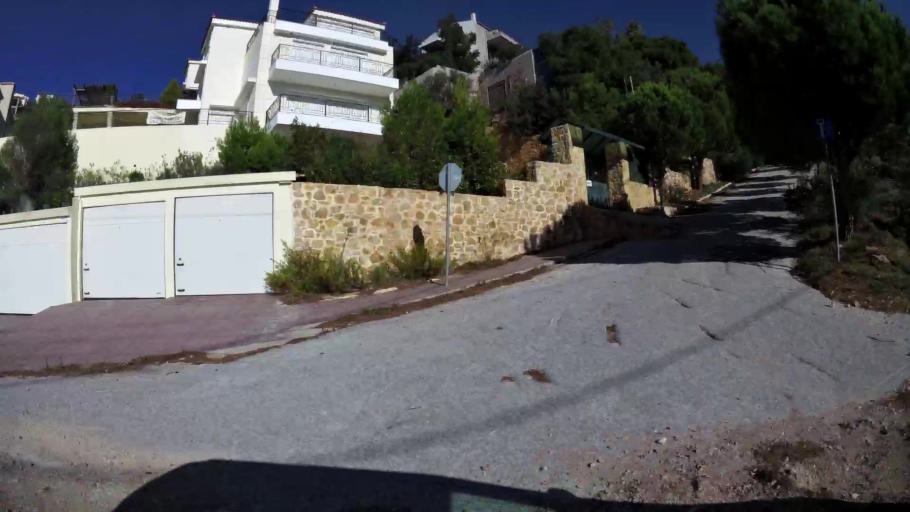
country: GR
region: Attica
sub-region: Nomarchia Anatolikis Attikis
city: Dhrafi
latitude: 38.0352
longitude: 23.8948
